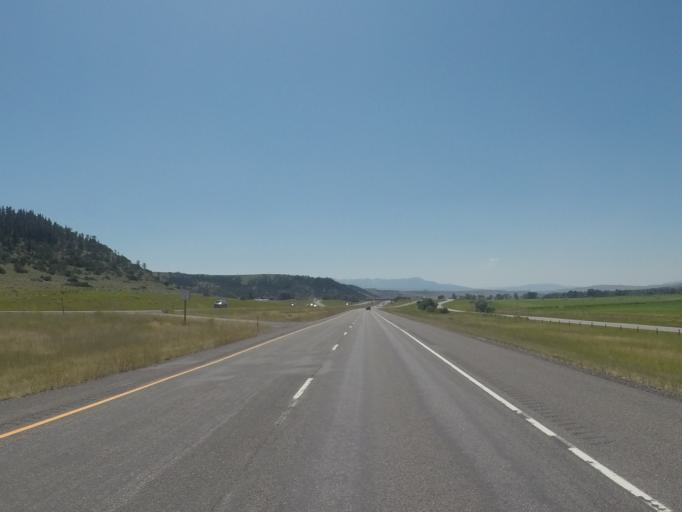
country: US
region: Montana
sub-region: Sweet Grass County
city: Big Timber
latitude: 45.7832
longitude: -110.0572
